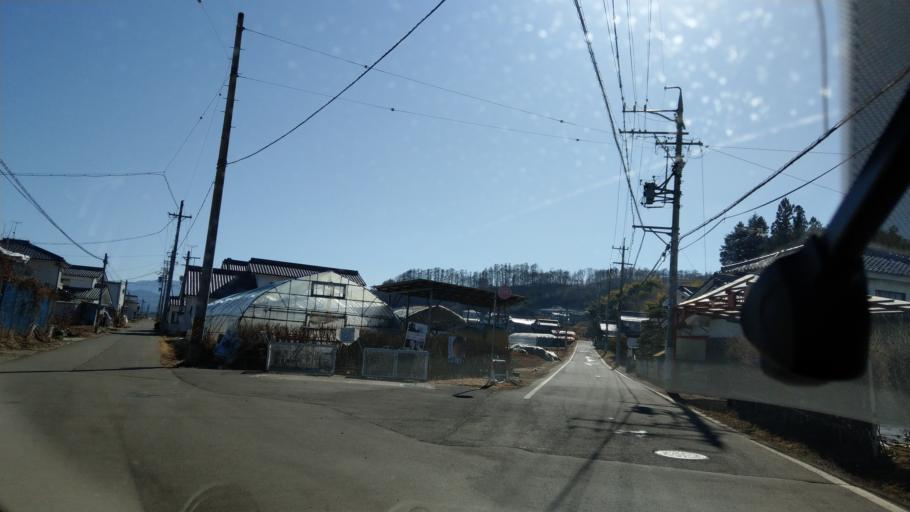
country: JP
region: Nagano
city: Saku
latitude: 36.2243
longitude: 138.4455
